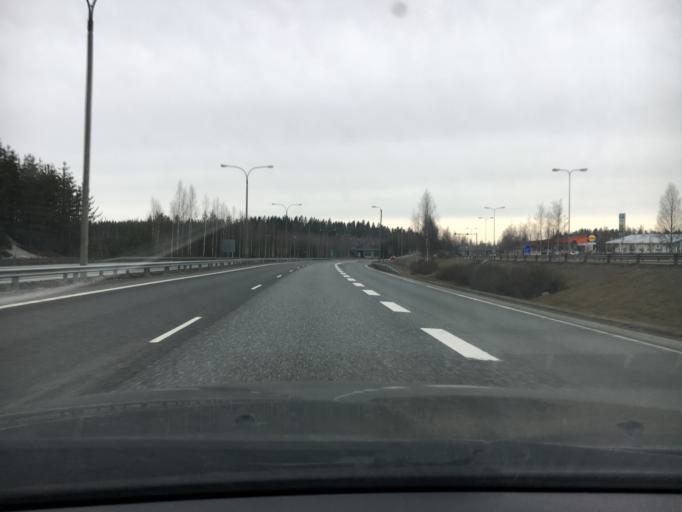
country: FI
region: Northern Savo
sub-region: Kuopio
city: Siilinjaervi
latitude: 63.0704
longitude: 27.6594
